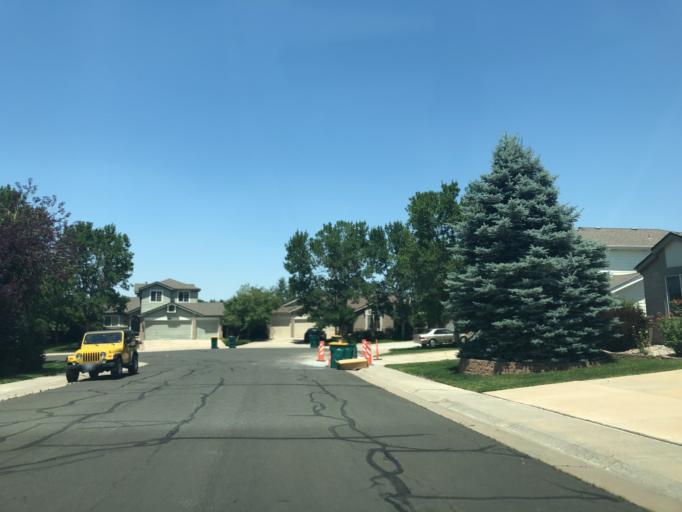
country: US
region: Colorado
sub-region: Arapahoe County
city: Dove Valley
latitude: 39.6305
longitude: -104.7638
